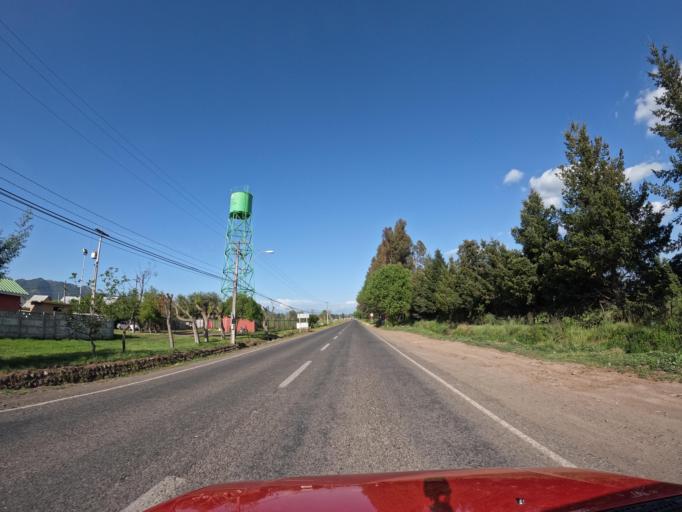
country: CL
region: Maule
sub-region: Provincia de Curico
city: Rauco
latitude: -34.8684
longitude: -71.2596
